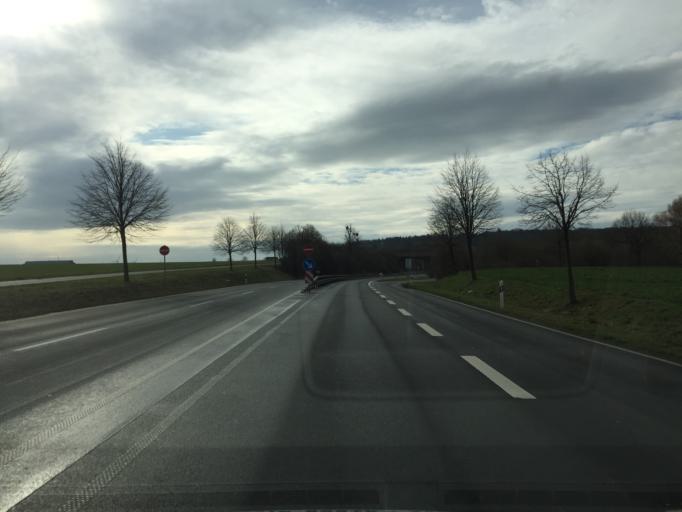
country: DE
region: Lower Saxony
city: Wennigsen
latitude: 52.2486
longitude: 9.6344
